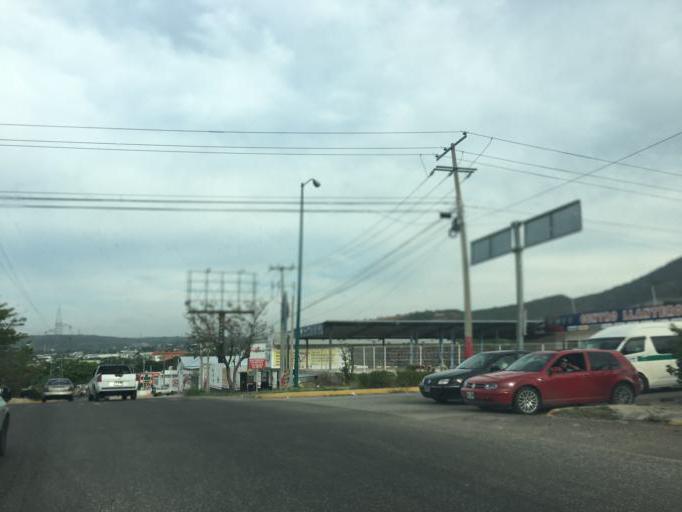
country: MX
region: Chiapas
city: Tuxtla Gutierrez
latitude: 16.7758
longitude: -93.1736
